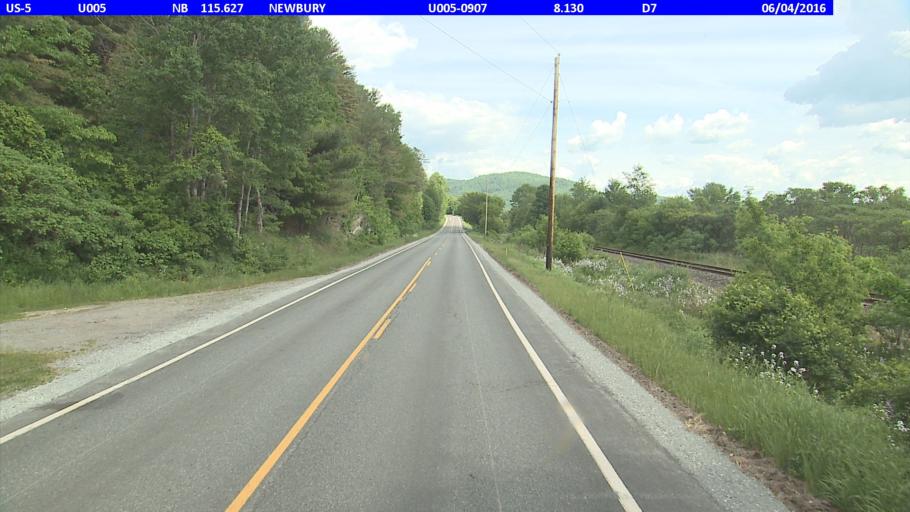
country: US
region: New Hampshire
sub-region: Grafton County
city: Woodsville
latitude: 44.1351
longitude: -72.0430
